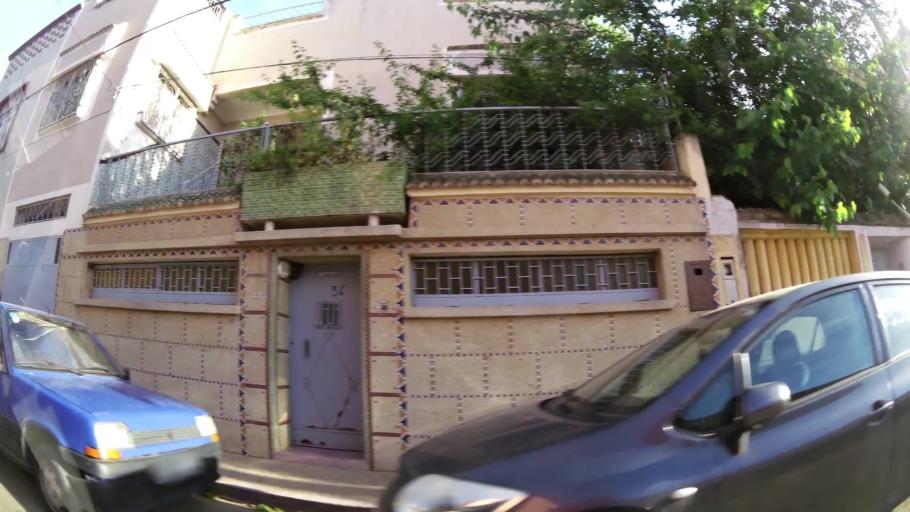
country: MA
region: Oriental
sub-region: Oujda-Angad
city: Oujda
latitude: 34.6760
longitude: -1.9103
